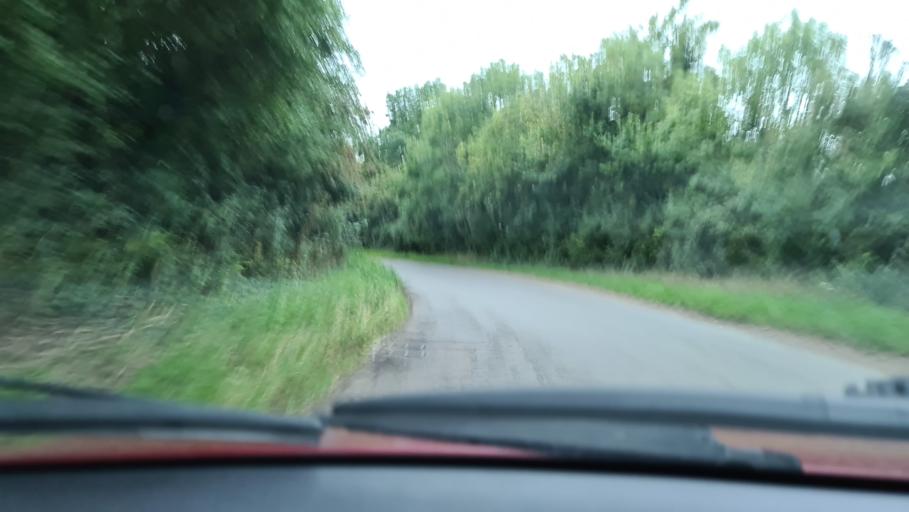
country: GB
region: England
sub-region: Oxfordshire
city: Somerton
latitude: 51.9594
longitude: -1.3011
